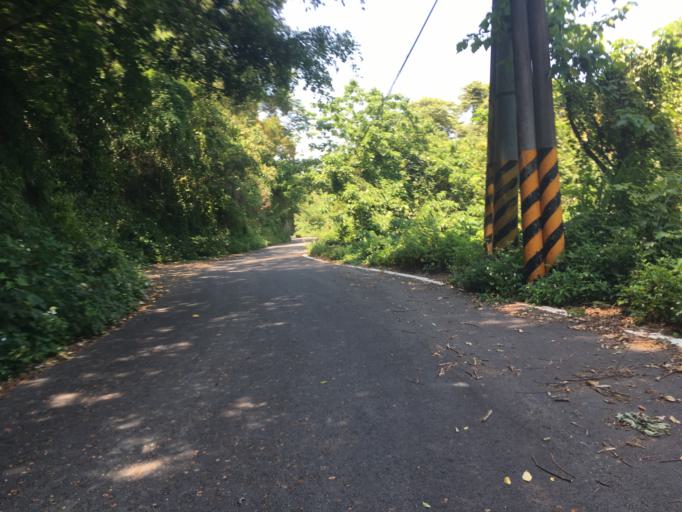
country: TW
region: Taiwan
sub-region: Hsinchu
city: Hsinchu
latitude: 24.7334
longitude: 120.9803
